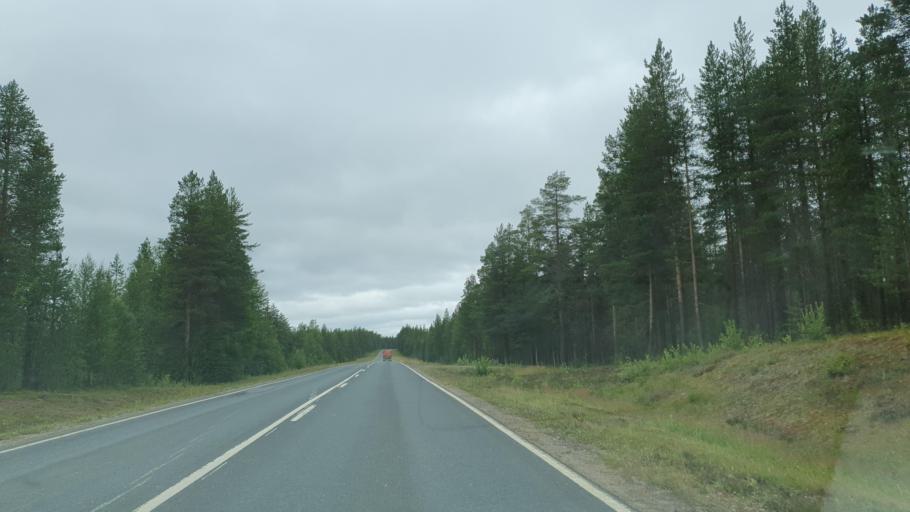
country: FI
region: Lapland
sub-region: Pohjois-Lappi
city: Sodankylae
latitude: 67.4151
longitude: 26.4883
